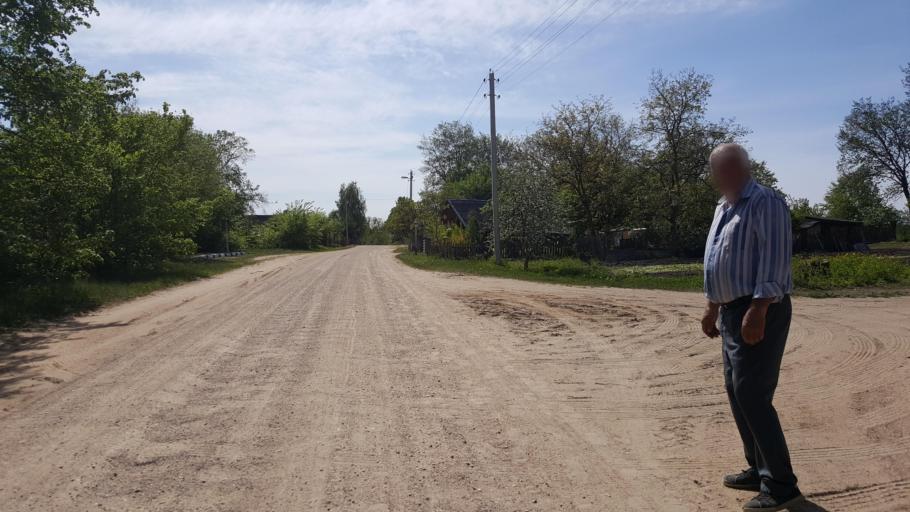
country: BY
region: Brest
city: Zhabinka
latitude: 52.3457
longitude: 24.1295
